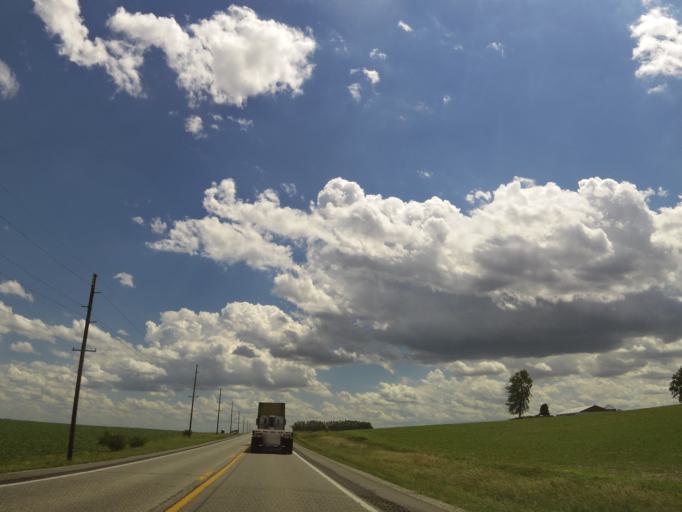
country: US
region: Iowa
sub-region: Benton County
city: Urbana
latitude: 42.2798
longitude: -91.8900
